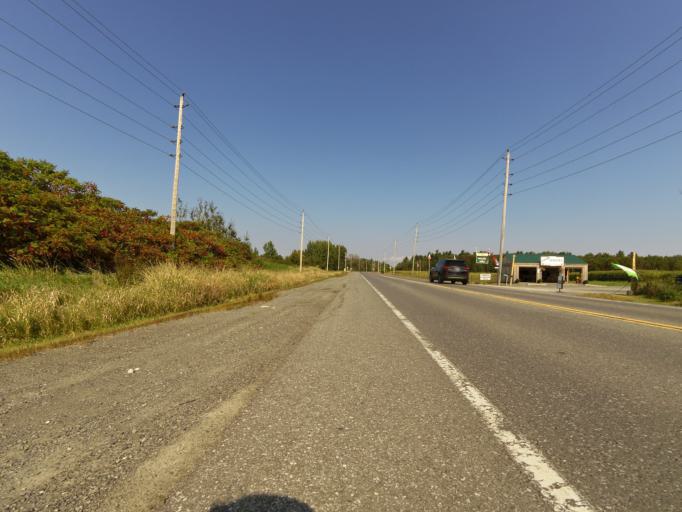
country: CA
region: Ontario
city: Bells Corners
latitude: 45.3169
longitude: -75.8022
